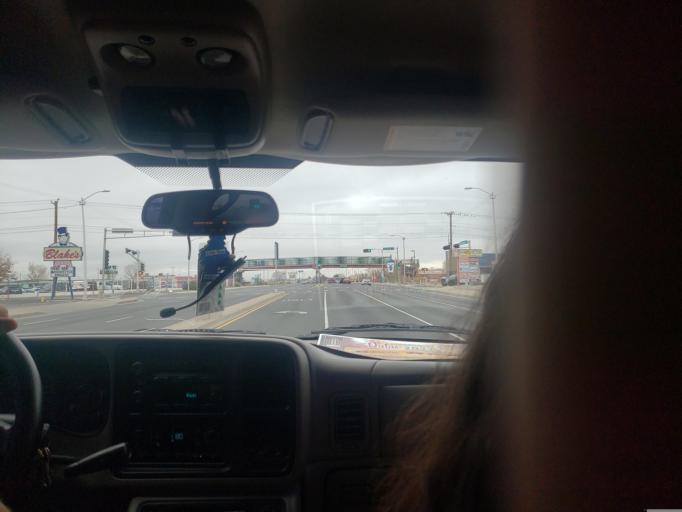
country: US
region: New Mexico
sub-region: Bernalillo County
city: Albuquerque
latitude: 35.0937
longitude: -106.7097
